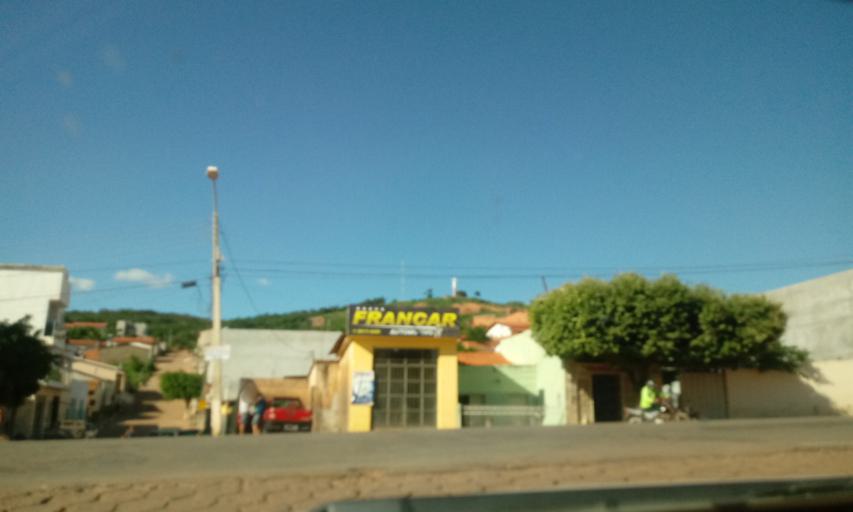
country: BR
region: Bahia
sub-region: Riacho De Santana
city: Riacho de Santana
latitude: -13.7700
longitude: -42.7152
